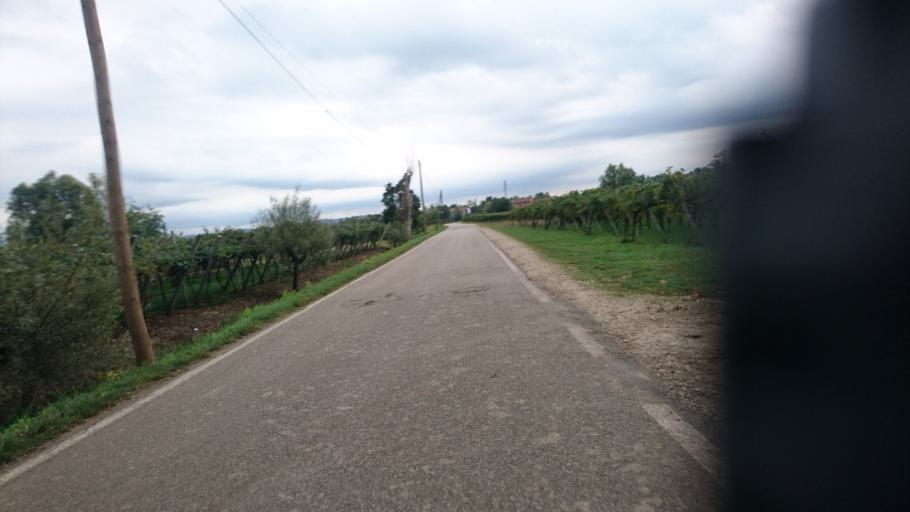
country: IT
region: Veneto
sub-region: Provincia di Vicenza
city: Gambellara
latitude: 45.4373
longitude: 11.3405
